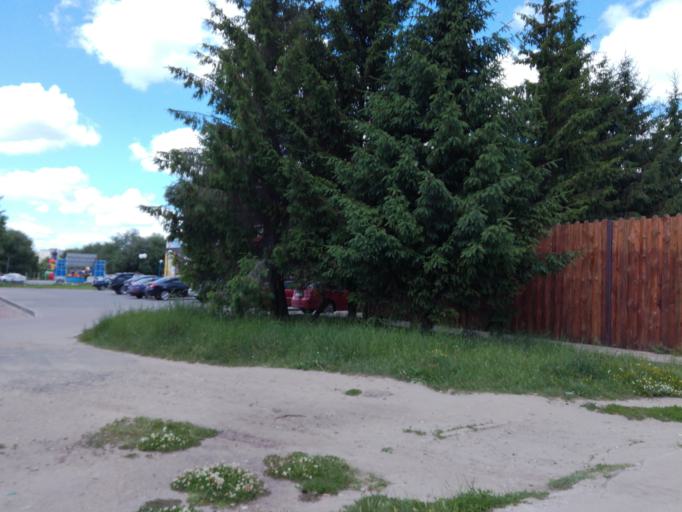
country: RU
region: Kursk
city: Kursk
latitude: 51.7464
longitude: 36.2547
